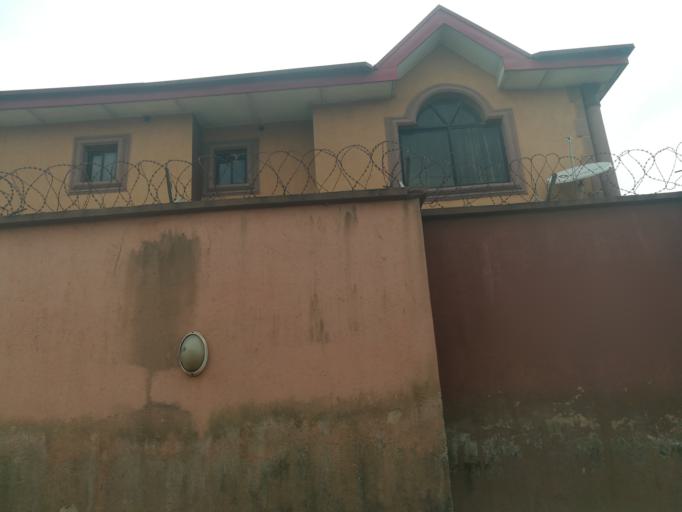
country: NG
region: Lagos
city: Ikorodu
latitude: 6.6201
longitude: 3.5210
